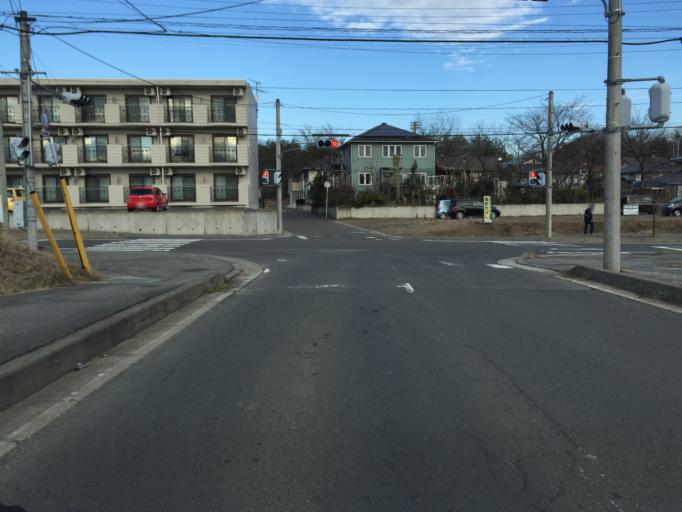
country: JP
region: Fukushima
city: Fukushima-shi
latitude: 37.6787
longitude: 140.4549
